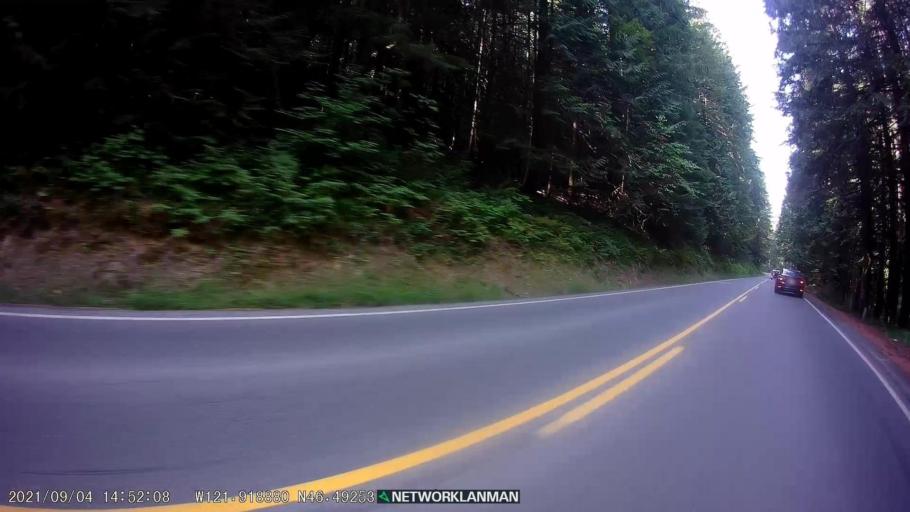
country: US
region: Washington
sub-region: Lewis County
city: Morton
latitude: 46.4926
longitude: -121.9189
